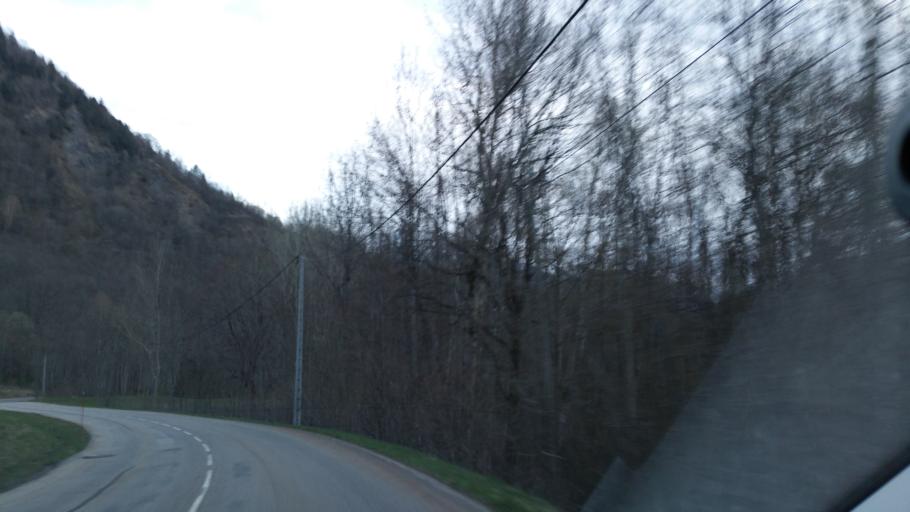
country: FR
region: Rhone-Alpes
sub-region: Departement de la Savoie
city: La Chambre
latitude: 45.3834
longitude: 6.3292
